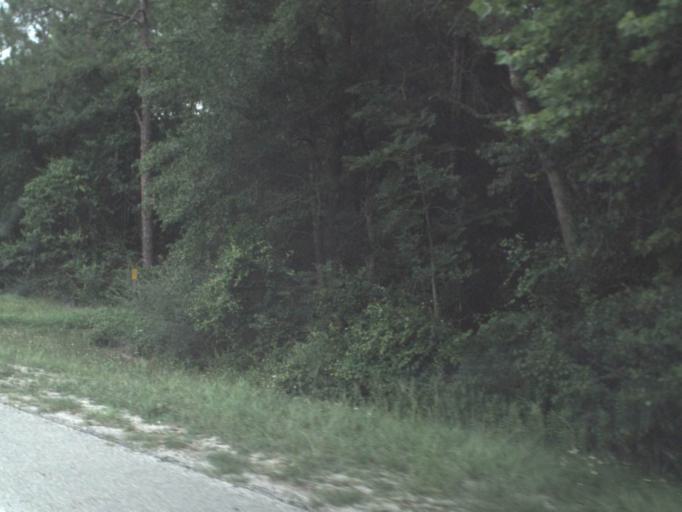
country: US
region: Florida
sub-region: Bradford County
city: Starke
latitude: 30.0610
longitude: -82.0660
